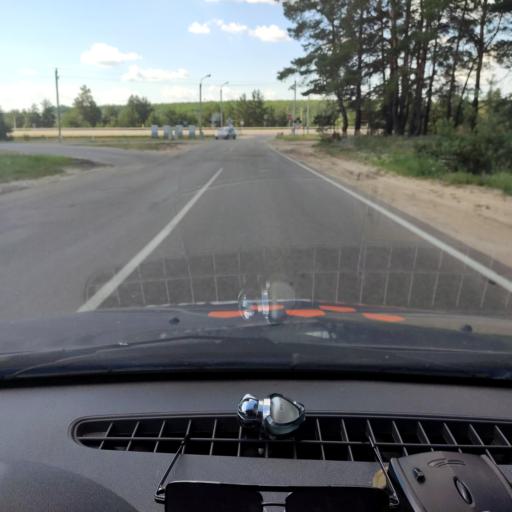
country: RU
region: Voronezj
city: Novovoronezh
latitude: 51.3303
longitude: 39.2543
